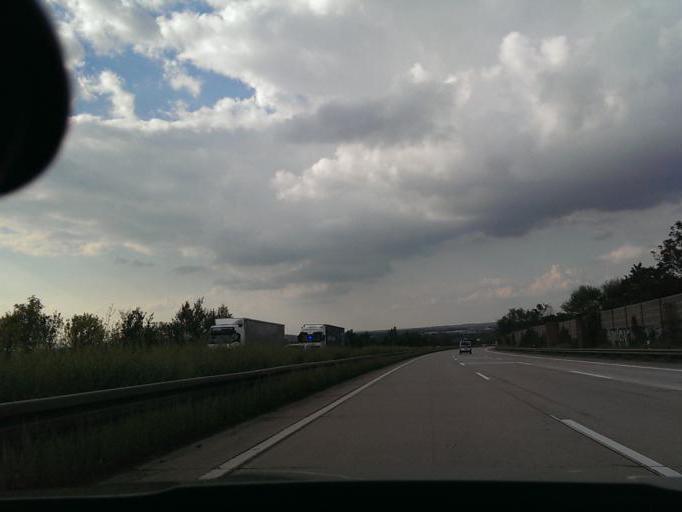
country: DE
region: Lower Saxony
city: Hildesheim
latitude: 52.1424
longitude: 10.0005
